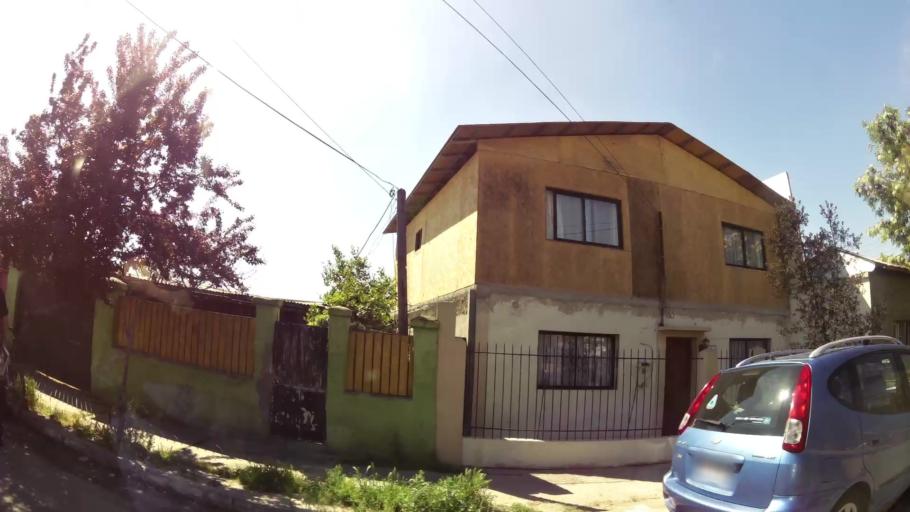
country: CL
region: Santiago Metropolitan
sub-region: Provincia de Santiago
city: Santiago
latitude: -33.5111
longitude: -70.6409
